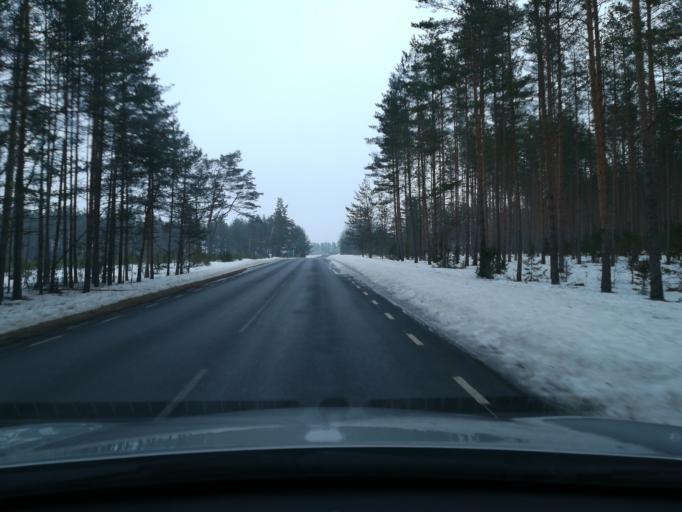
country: EE
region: Harju
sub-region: Kuusalu vald
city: Kuusalu
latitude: 59.4648
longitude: 25.5047
